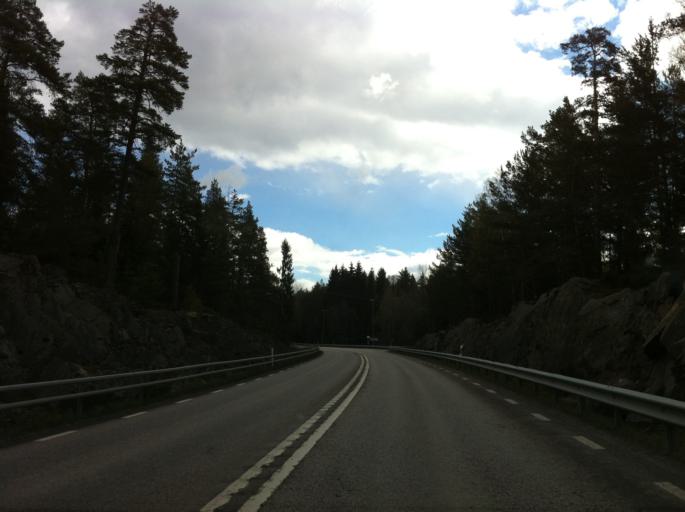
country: SE
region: Stockholm
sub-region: Vallentuna Kommun
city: Vallentuna
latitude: 59.5126
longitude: 18.1764
